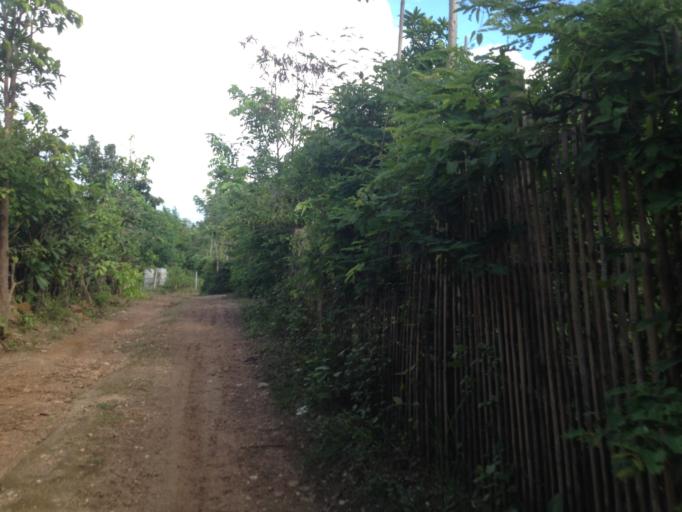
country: TH
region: Chiang Mai
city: Hang Dong
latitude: 18.7025
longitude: 98.8920
